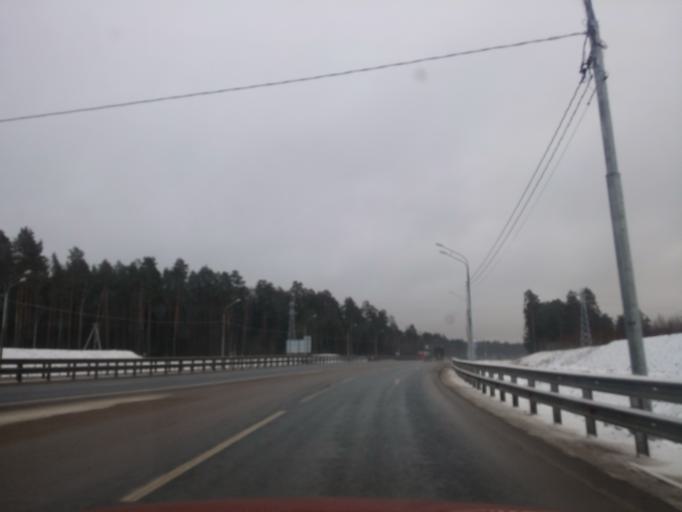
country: RU
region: Tverskaya
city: Likhoslavl'
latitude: 56.9438
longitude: 35.5024
